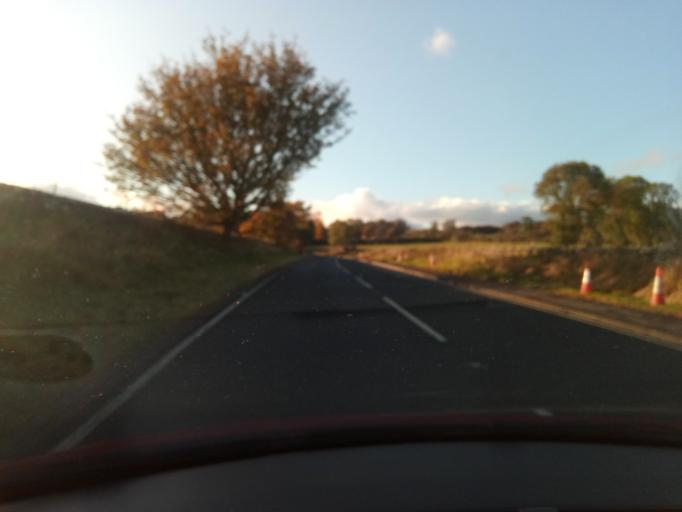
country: GB
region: England
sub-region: County Durham
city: Stanhope
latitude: 54.7492
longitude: -2.0219
